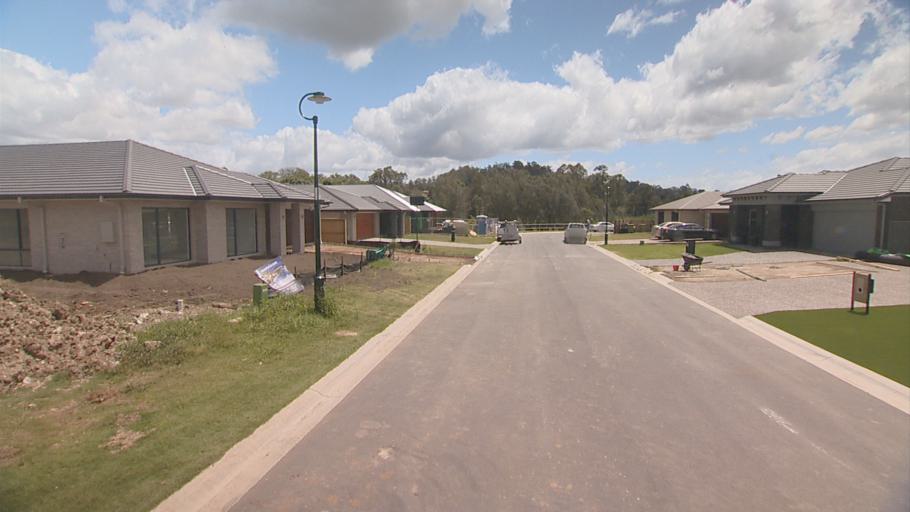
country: AU
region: Queensland
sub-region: Logan
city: Waterford West
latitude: -27.6832
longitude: 153.1708
